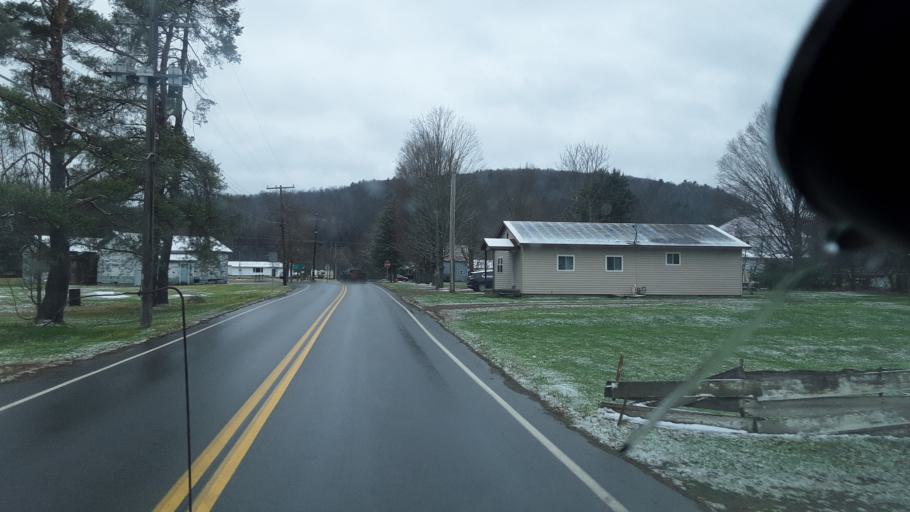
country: US
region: Pennsylvania
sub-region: Potter County
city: Shinglehouse
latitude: 41.9658
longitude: -78.1870
